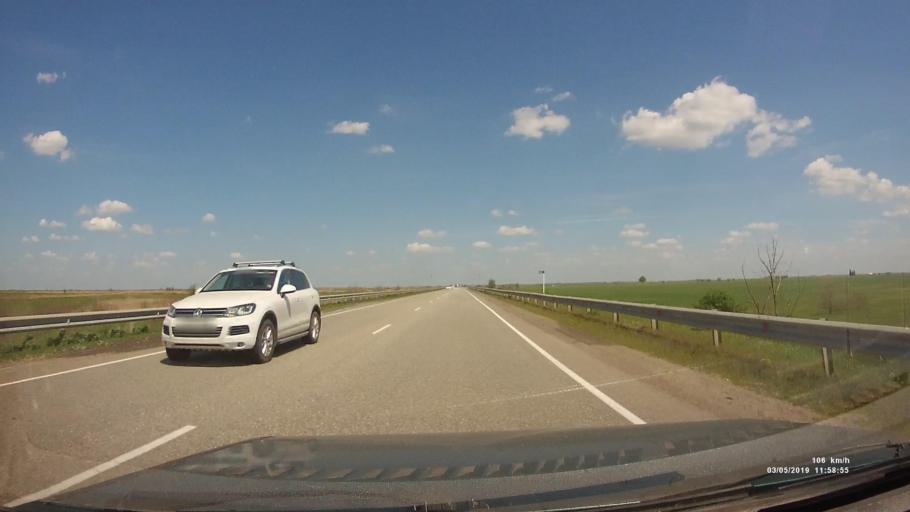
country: RU
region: Rostov
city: Bagayevskaya
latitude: 47.2276
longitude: 40.3250
